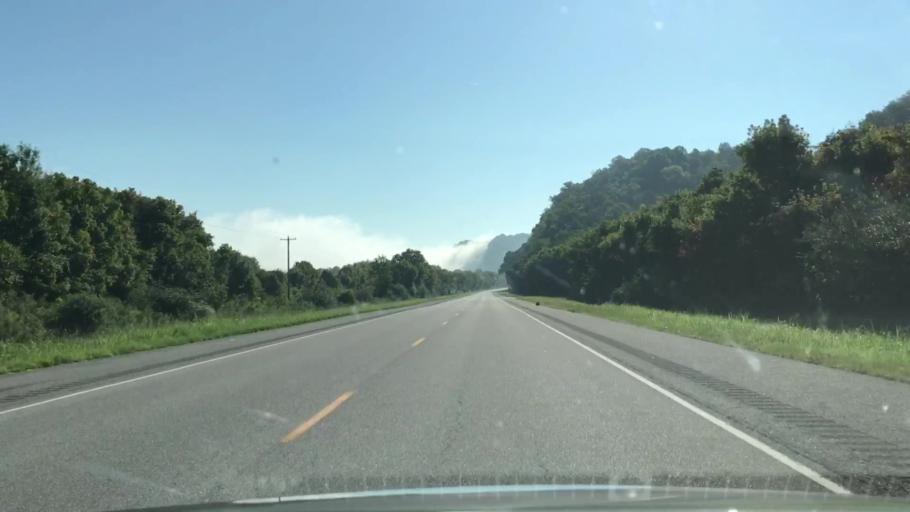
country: US
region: Tennessee
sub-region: Jackson County
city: Gainesboro
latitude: 36.4379
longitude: -85.6099
